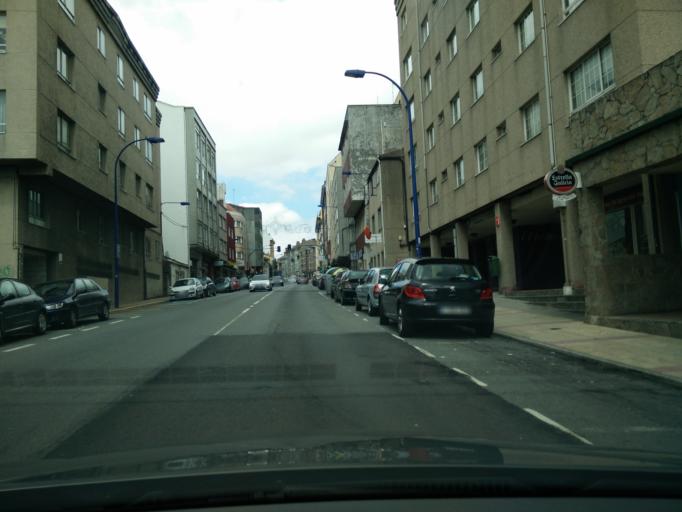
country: ES
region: Galicia
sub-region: Provincia da Coruna
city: Culleredo
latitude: 43.3146
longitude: -8.3834
